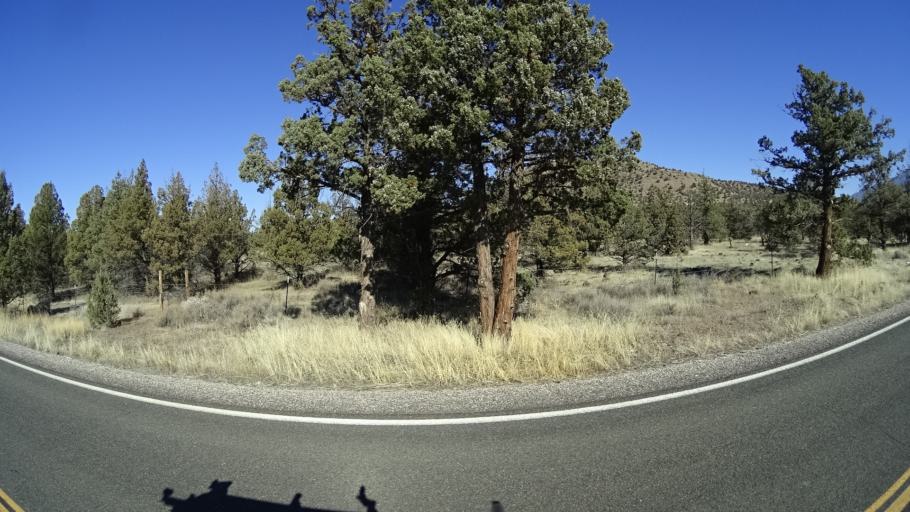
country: US
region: California
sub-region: Siskiyou County
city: Montague
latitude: 41.6599
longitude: -122.3918
